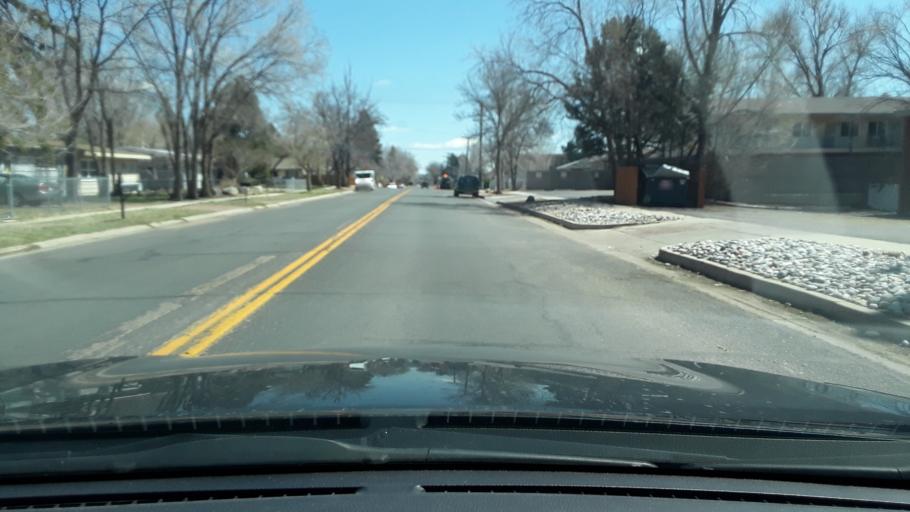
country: US
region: Colorado
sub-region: El Paso County
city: Colorado Springs
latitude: 38.8489
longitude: -104.7817
